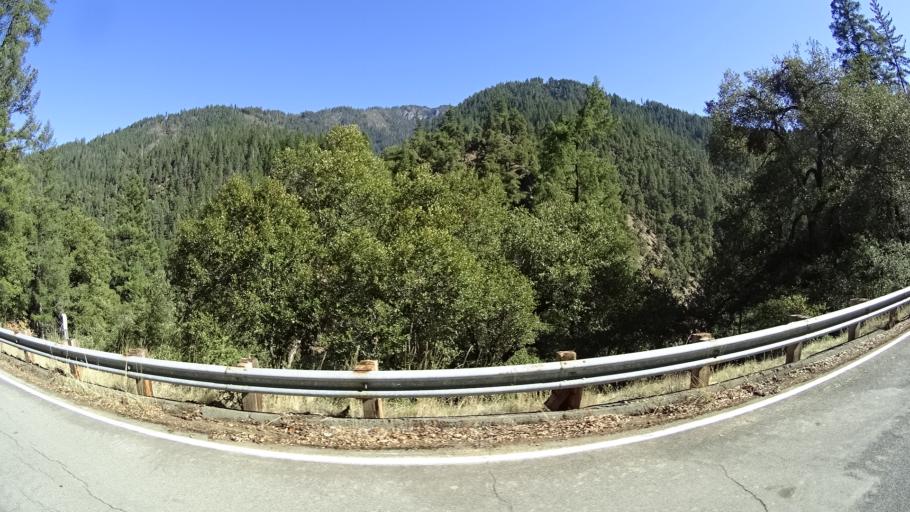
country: US
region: California
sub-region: Siskiyou County
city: Happy Camp
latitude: 41.3623
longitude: -123.4153
